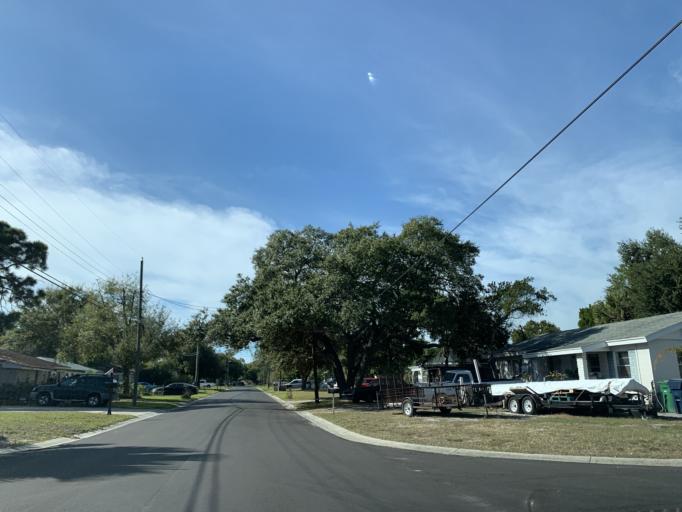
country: US
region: Florida
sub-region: Hillsborough County
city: Tampa
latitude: 27.8854
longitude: -82.5082
